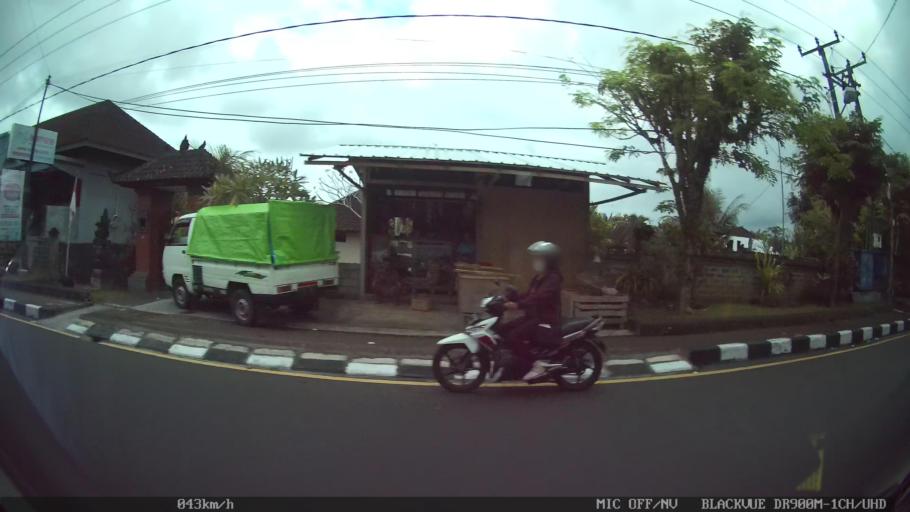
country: ID
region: Bali
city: Banjar Serangan
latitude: -8.5391
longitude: 115.1706
